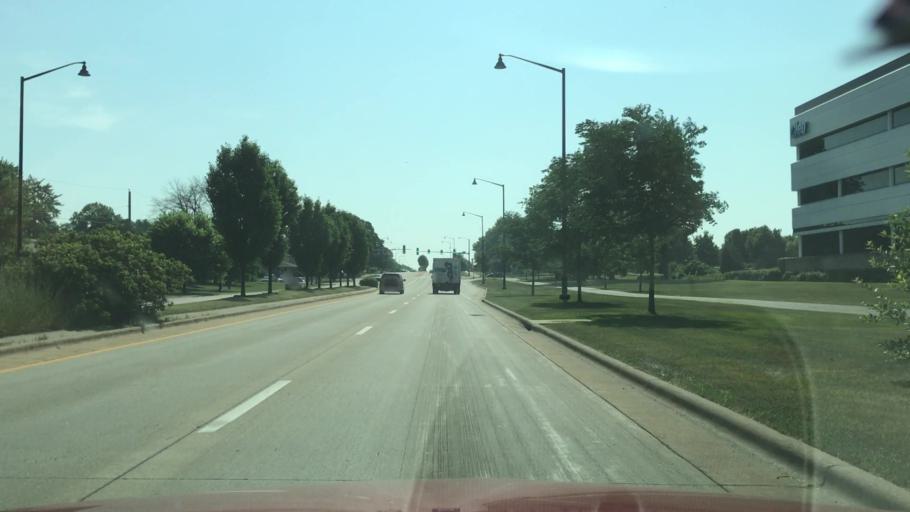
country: US
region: Illinois
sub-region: Winnebago County
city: Cherry Valley
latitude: 42.2382
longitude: -89.0218
